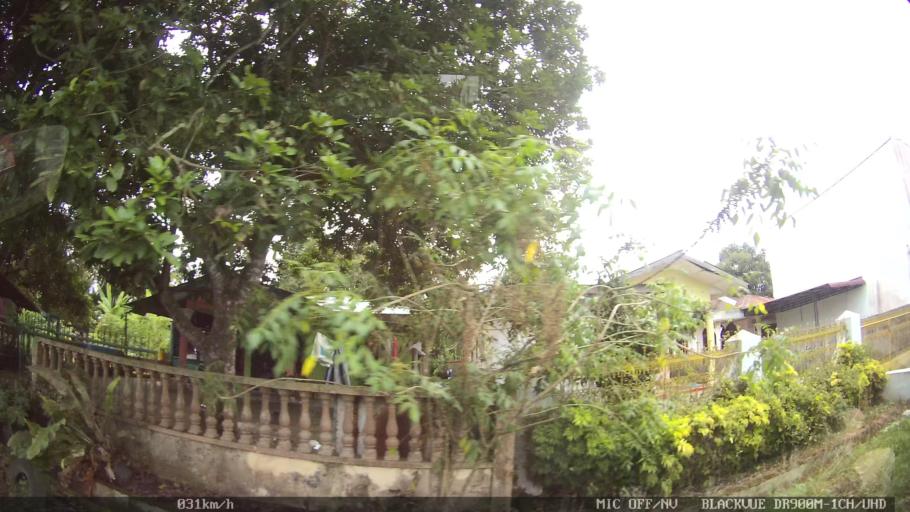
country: ID
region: North Sumatra
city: Sunggal
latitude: 3.6256
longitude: 98.5905
